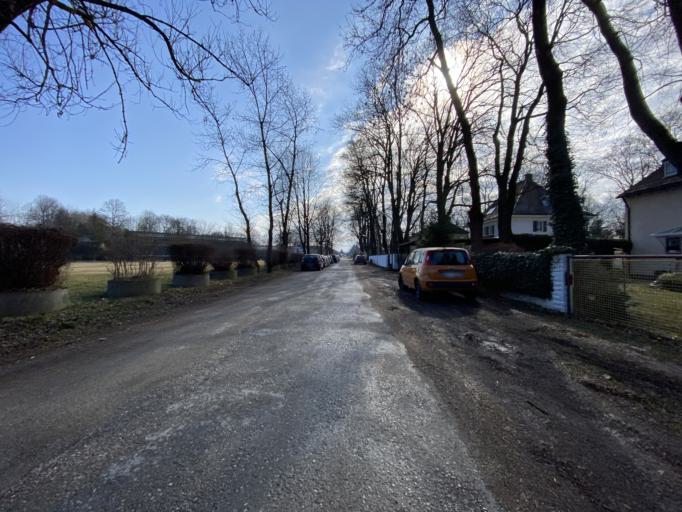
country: DE
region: Bavaria
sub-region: Upper Bavaria
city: Aschheim
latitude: 48.1446
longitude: 11.6727
